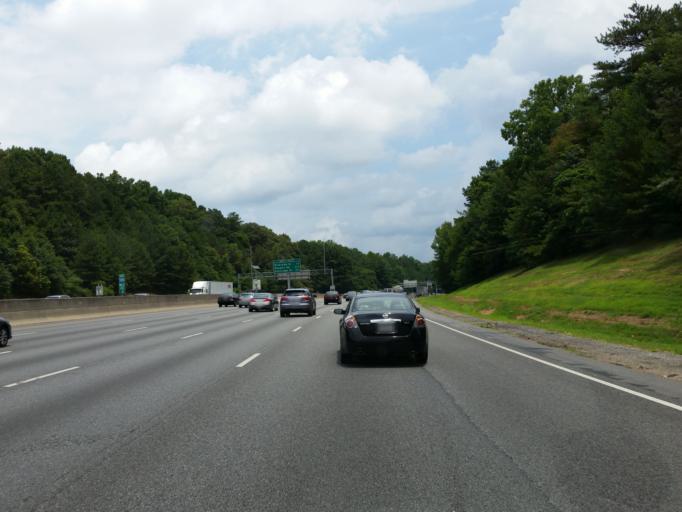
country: US
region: Georgia
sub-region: Fulton County
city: Sandy Springs
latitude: 33.9126
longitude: -84.4246
